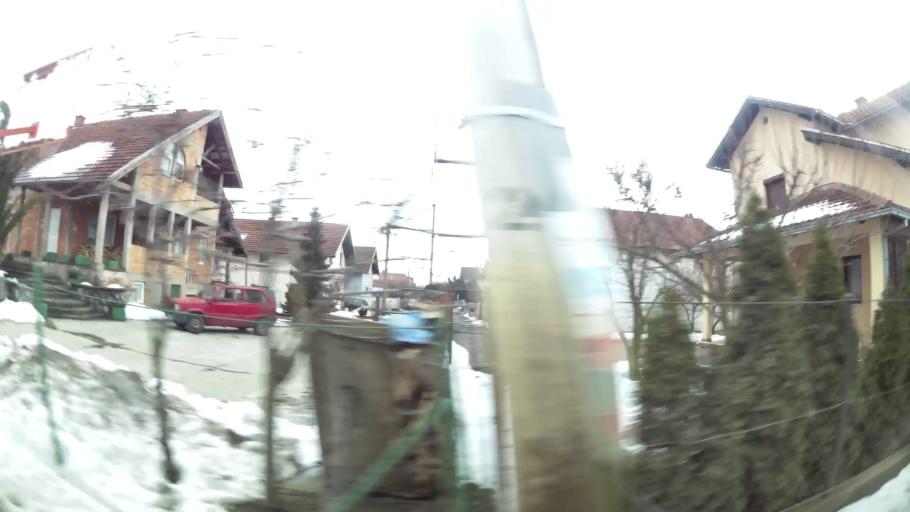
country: RS
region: Central Serbia
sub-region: Belgrade
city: Surcin
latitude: 44.8027
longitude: 20.3227
